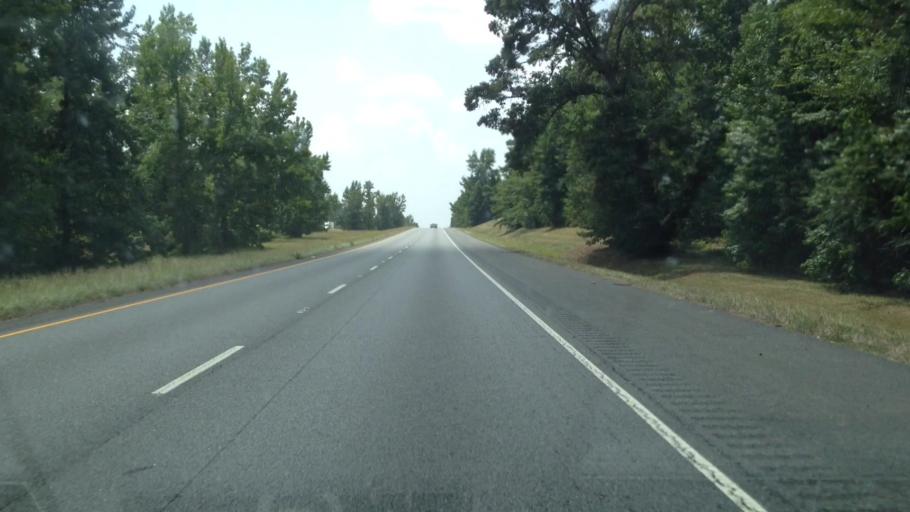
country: US
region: Louisiana
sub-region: Lincoln Parish
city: Grambling
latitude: 32.5453
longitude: -92.7488
